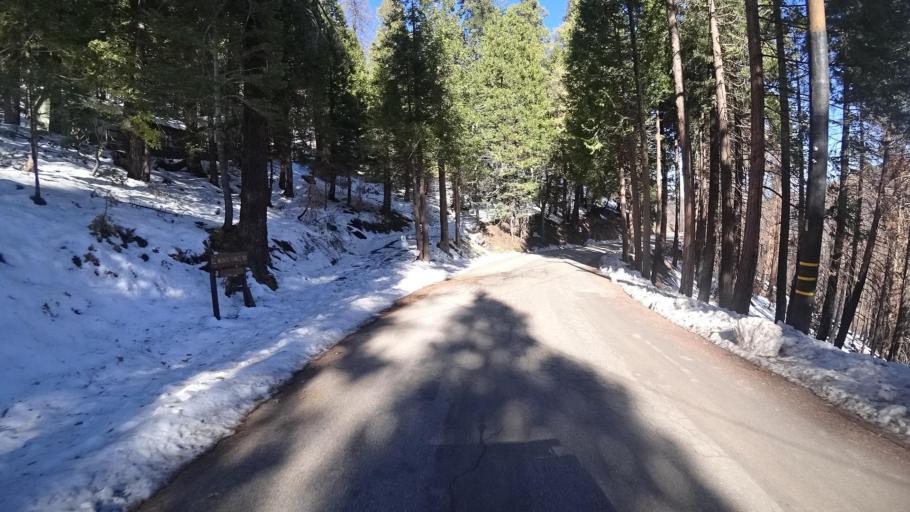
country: US
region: California
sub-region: Kern County
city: Alta Sierra
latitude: 35.7156
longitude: -118.5550
